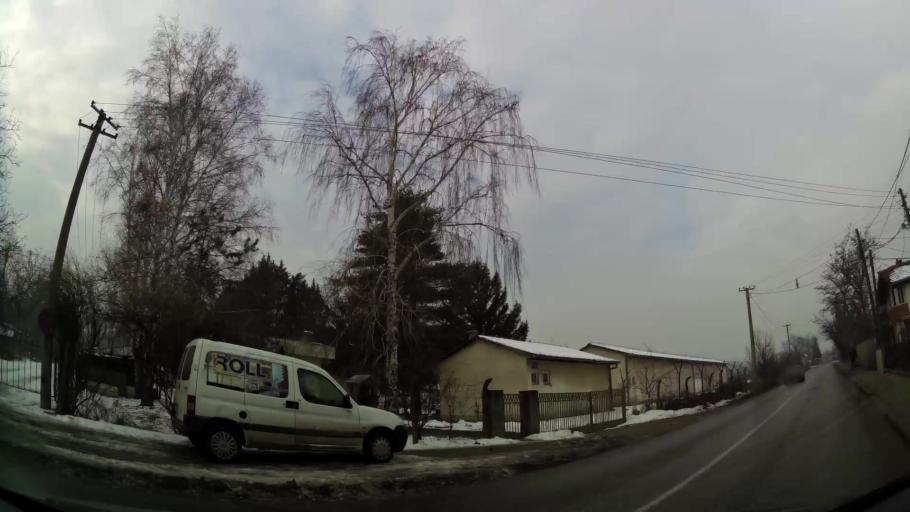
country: MK
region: Saraj
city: Saraj
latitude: 42.0227
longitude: 21.3500
